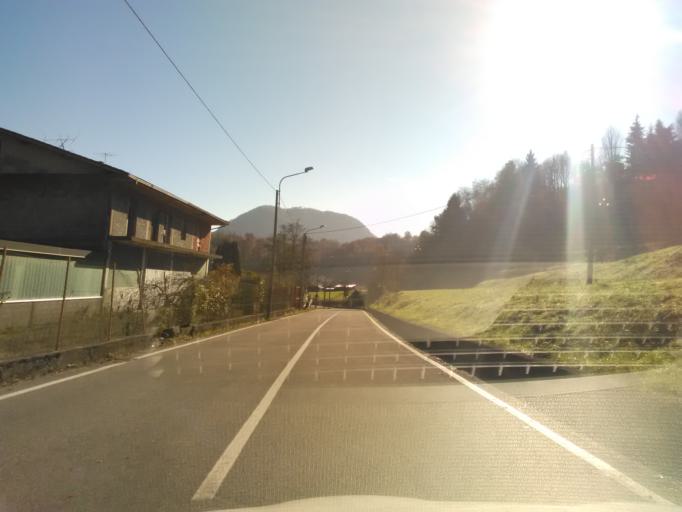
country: IT
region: Piedmont
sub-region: Provincia di Vercelli
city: Borgosesia
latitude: 45.7330
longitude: 8.2807
